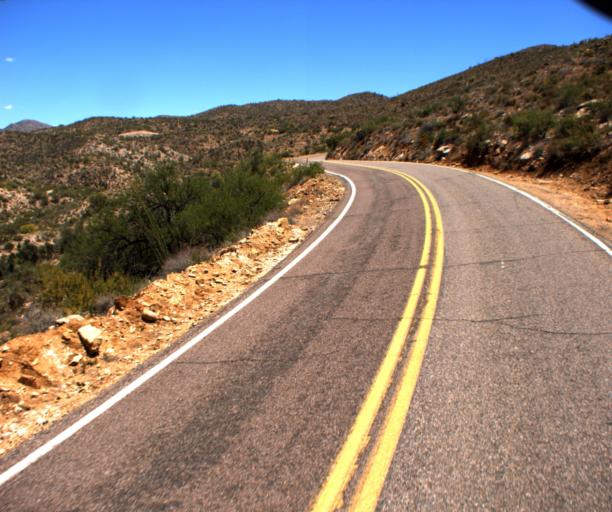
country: US
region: Arizona
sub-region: Yavapai County
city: Bagdad
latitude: 34.4591
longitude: -113.0229
